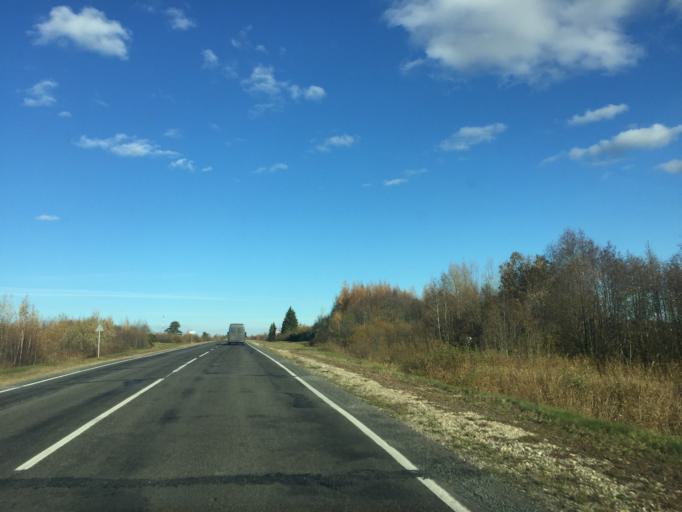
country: BY
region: Vitebsk
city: Dzisna
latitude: 55.2855
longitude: 28.1806
